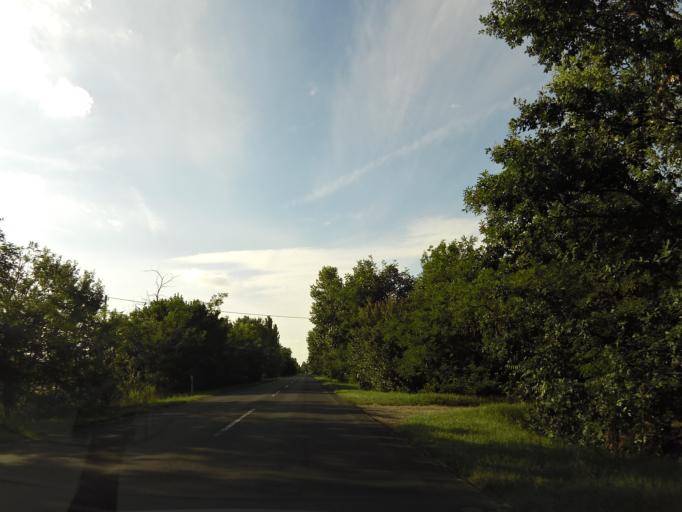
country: HU
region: Csongrad
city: Szatymaz
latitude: 46.3670
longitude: 20.0455
